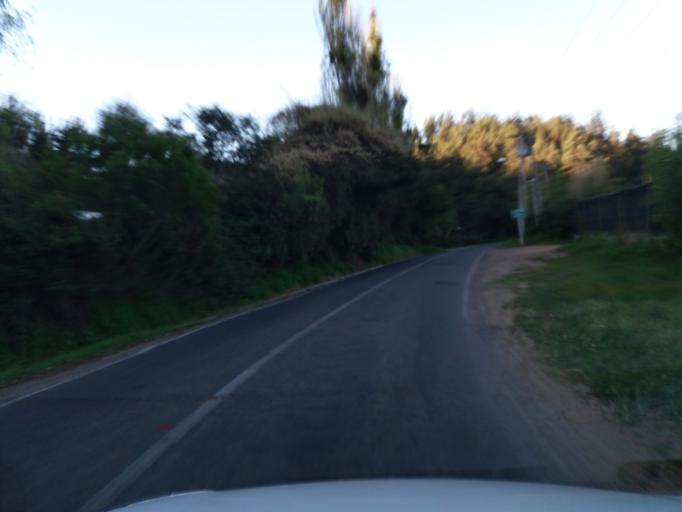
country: CL
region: Valparaiso
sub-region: Provincia de Quillota
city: Quillota
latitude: -32.8876
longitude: -71.2817
